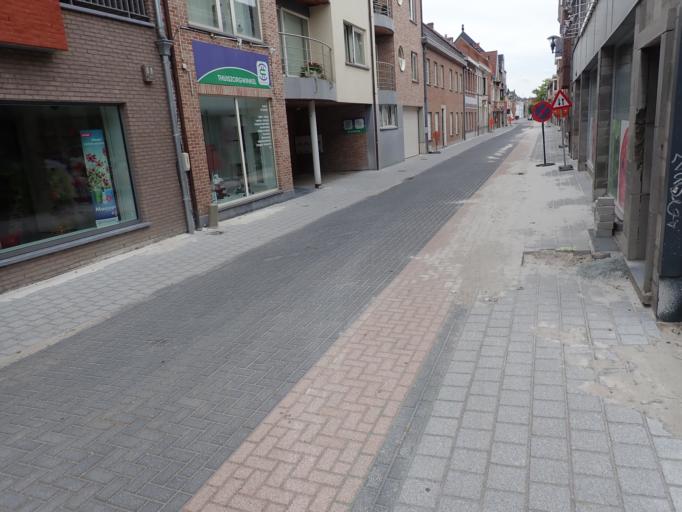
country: BE
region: Flanders
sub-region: Provincie Oost-Vlaanderen
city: Hamme
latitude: 51.0961
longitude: 4.1416
